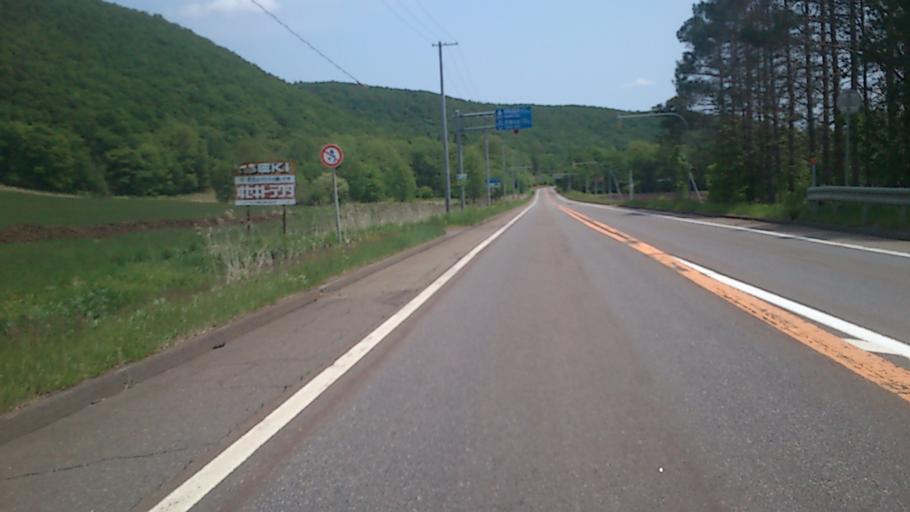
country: JP
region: Hokkaido
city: Otofuke
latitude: 43.2497
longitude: 143.4806
